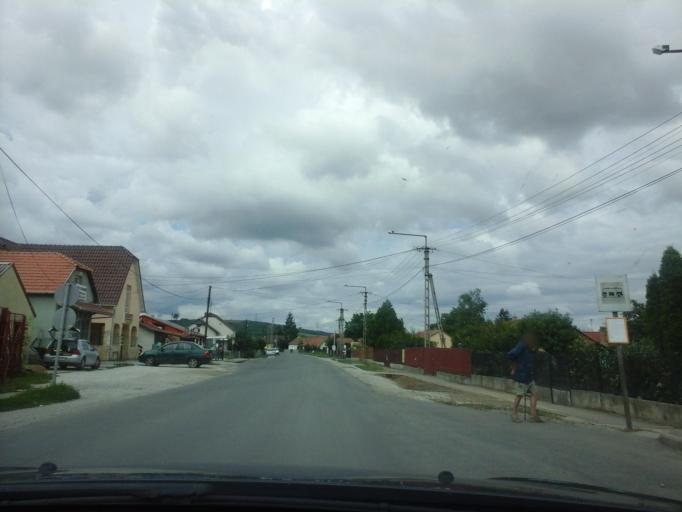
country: HU
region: Borsod-Abauj-Zemplen
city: Izsofalva
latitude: 48.2832
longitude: 20.6615
